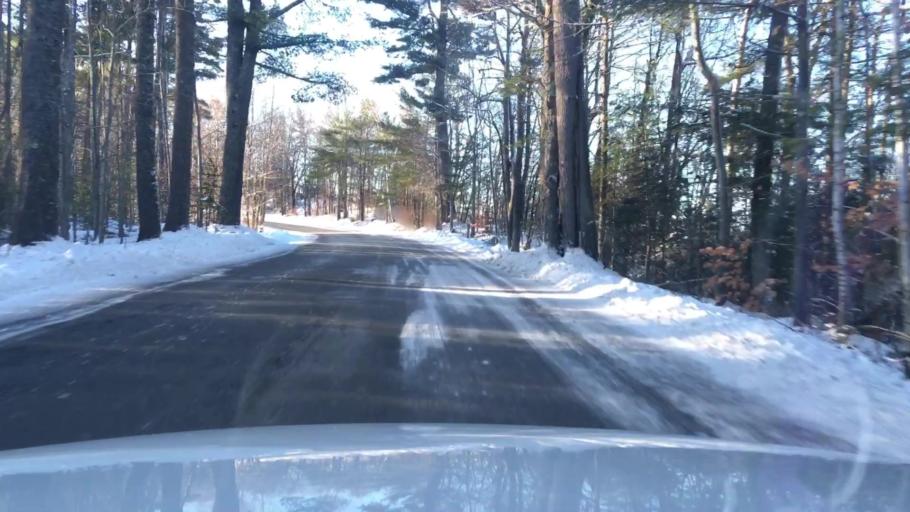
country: US
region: Maine
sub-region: Kennebec County
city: Belgrade
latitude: 44.4232
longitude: -69.8332
